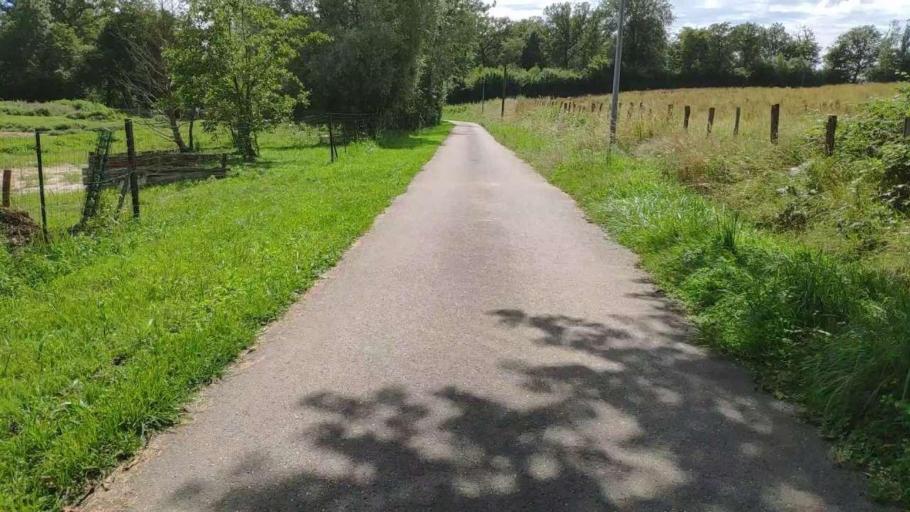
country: FR
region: Franche-Comte
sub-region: Departement du Jura
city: Bletterans
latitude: 46.8362
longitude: 5.4675
